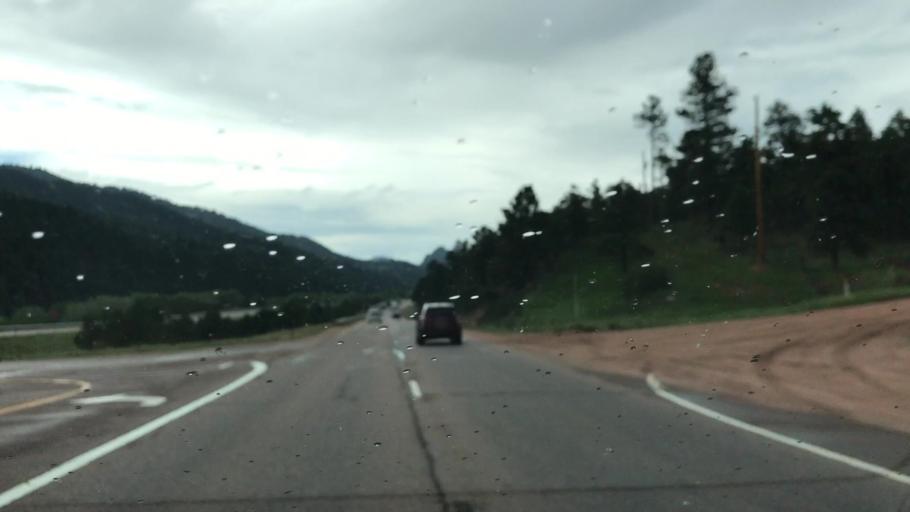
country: US
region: Colorado
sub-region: El Paso County
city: Cascade-Chipita Park
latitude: 38.9422
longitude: -105.0160
